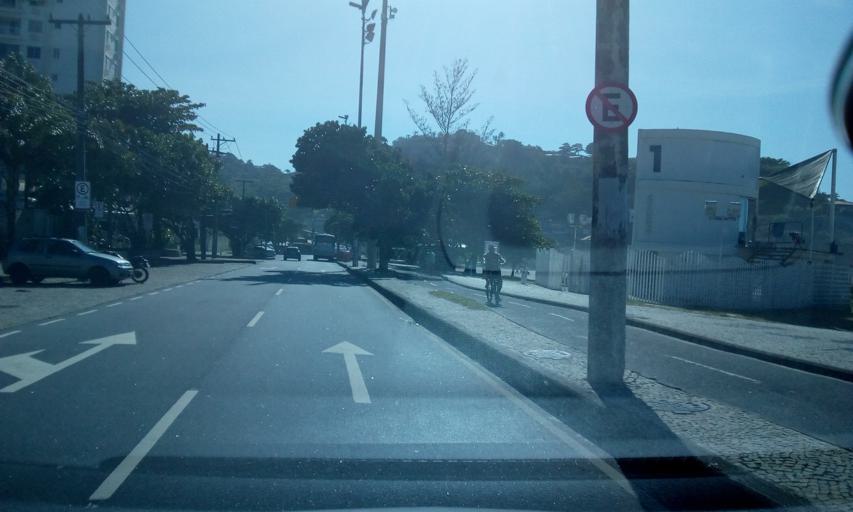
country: BR
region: Rio de Janeiro
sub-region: Rio De Janeiro
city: Rio de Janeiro
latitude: -23.0144
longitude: -43.2998
